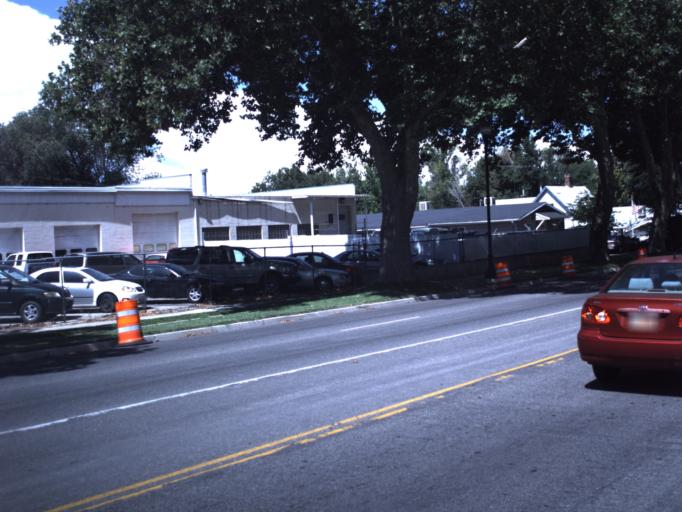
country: US
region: Utah
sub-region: Box Elder County
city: Brigham City
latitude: 41.5190
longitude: -112.0155
